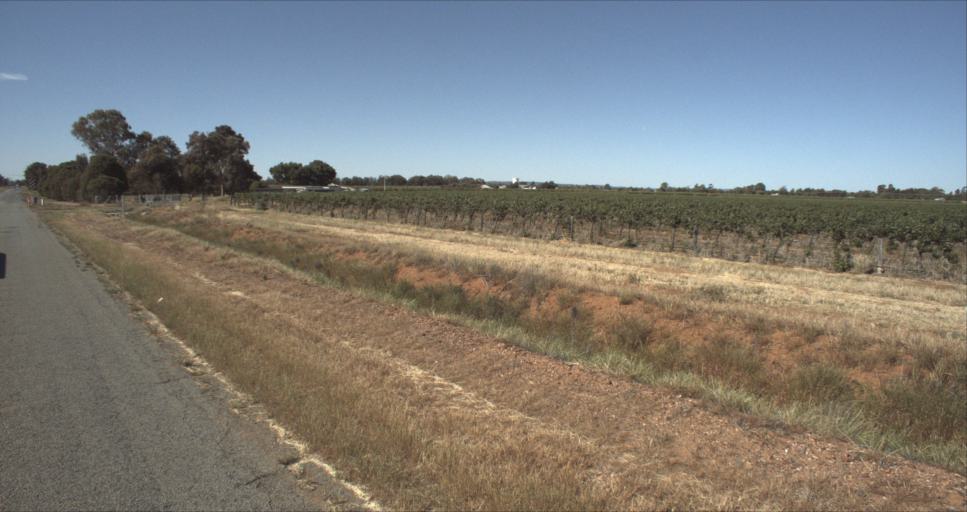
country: AU
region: New South Wales
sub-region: Leeton
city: Leeton
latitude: -34.5704
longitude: 146.3818
